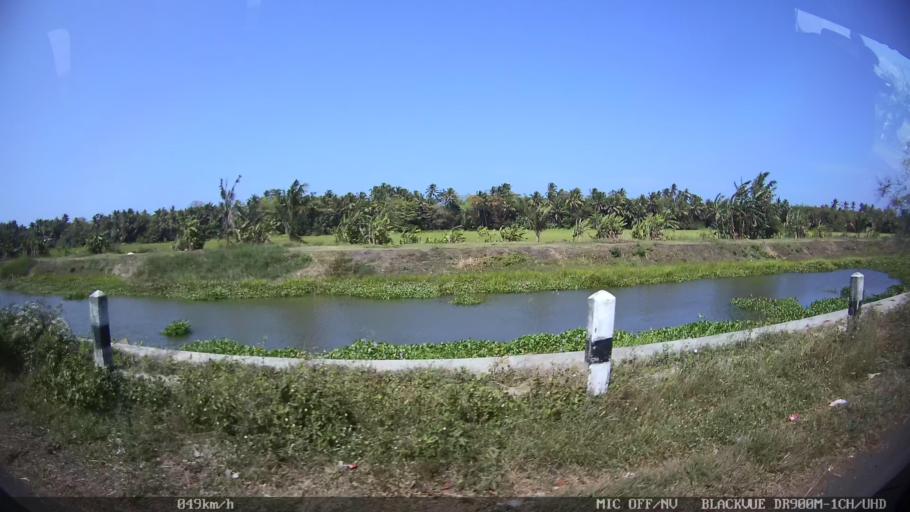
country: ID
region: Daerah Istimewa Yogyakarta
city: Srandakan
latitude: -7.9469
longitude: 110.1782
